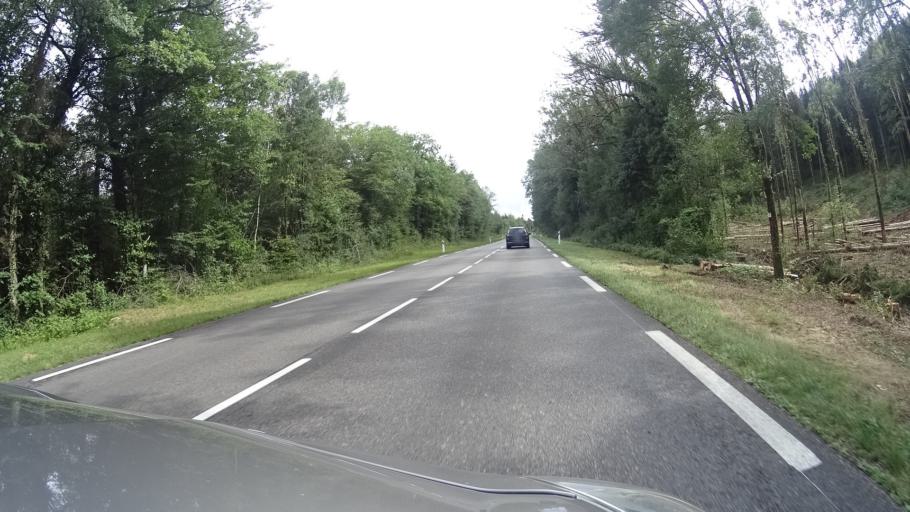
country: FR
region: Franche-Comte
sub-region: Departement du Jura
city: Champagnole
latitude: 46.7106
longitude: 5.9294
